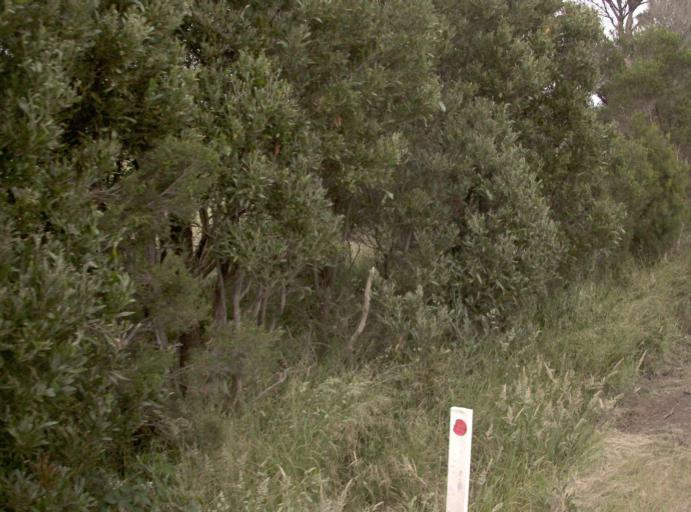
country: AU
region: Victoria
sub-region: Bass Coast
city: North Wonthaggi
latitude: -38.5559
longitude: 145.6387
